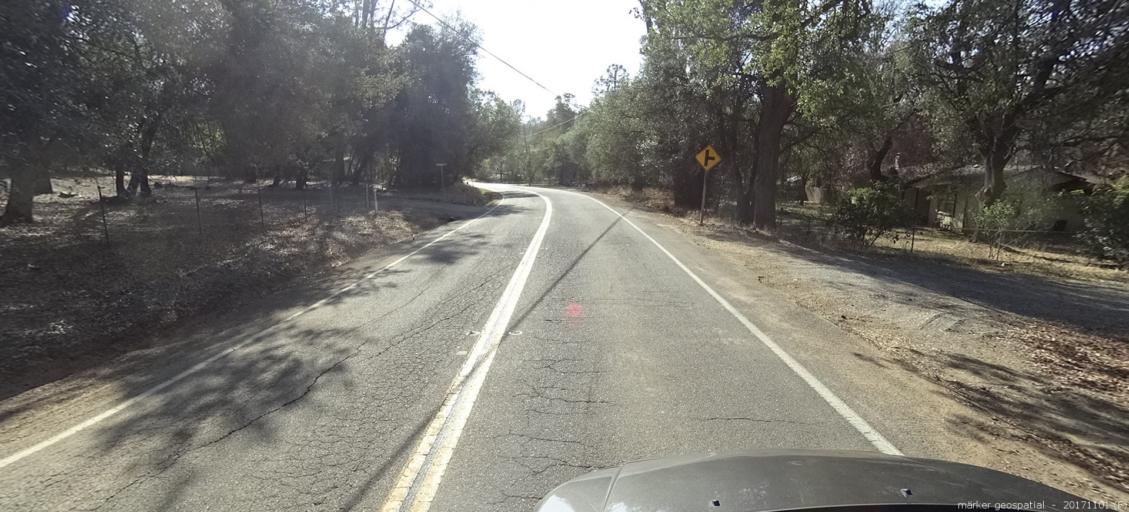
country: US
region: California
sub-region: Shasta County
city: Shasta Lake
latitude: 40.6900
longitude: -122.3181
